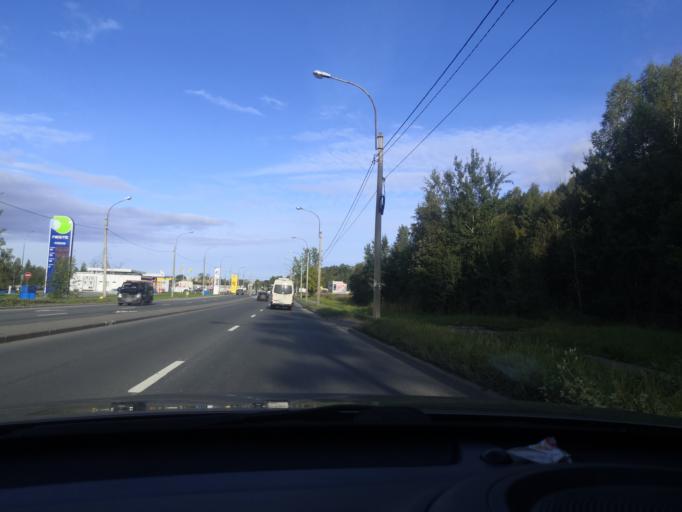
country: RU
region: St.-Petersburg
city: Pargolovo
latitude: 60.0764
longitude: 30.2736
